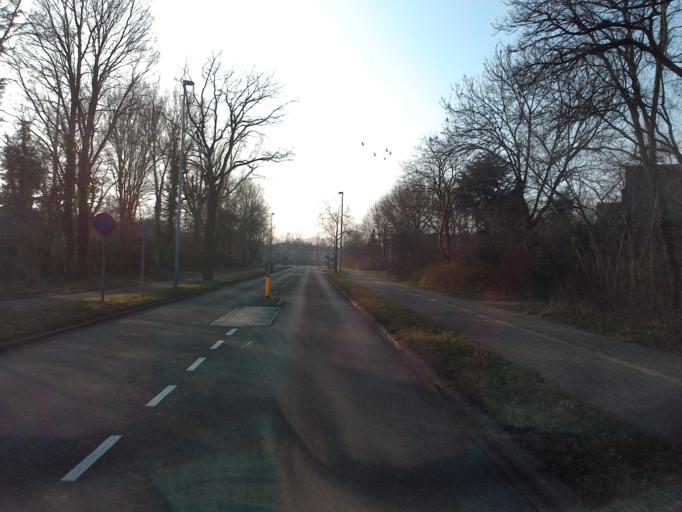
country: NL
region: Utrecht
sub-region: Gemeente Zeist
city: Zeist
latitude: 52.0772
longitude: 5.2263
